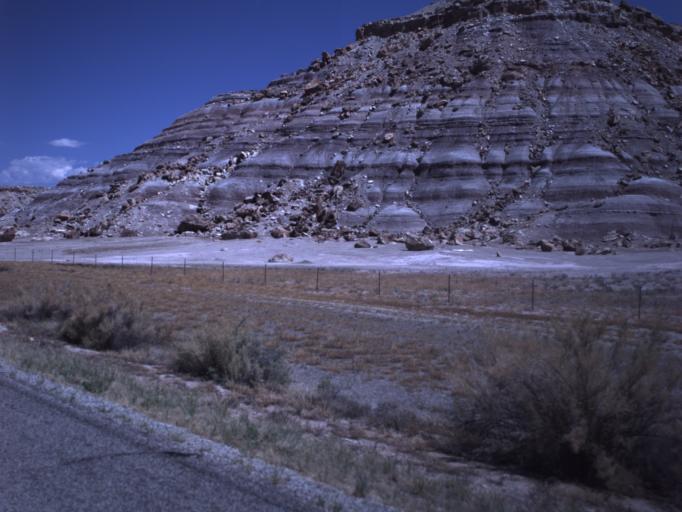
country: US
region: Utah
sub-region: Carbon County
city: East Carbon City
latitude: 38.9159
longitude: -110.3733
